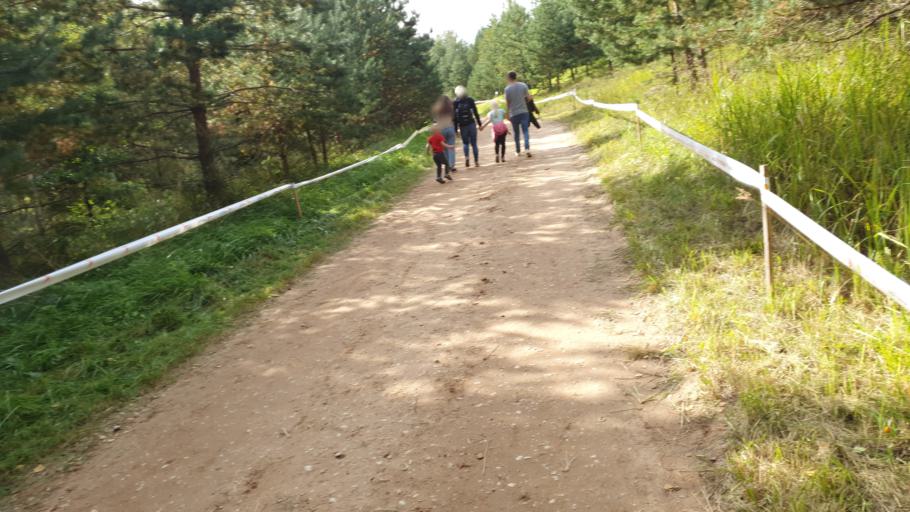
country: EE
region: Tartu
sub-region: UElenurme vald
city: Ulenurme
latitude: 58.1336
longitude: 26.7694
